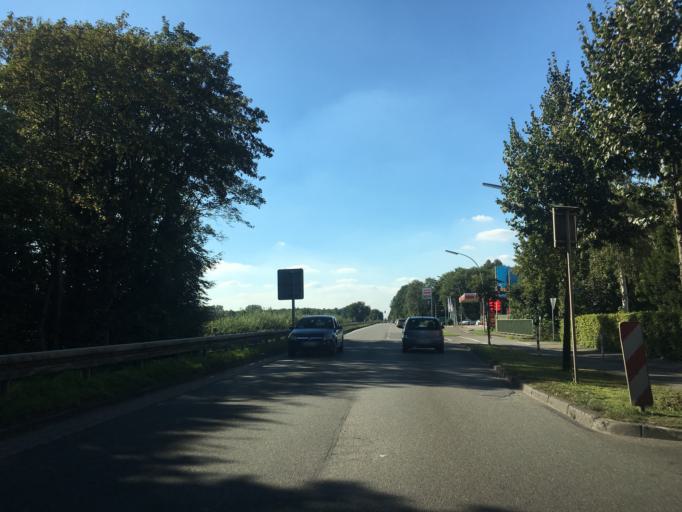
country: DE
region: North Rhine-Westphalia
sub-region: Regierungsbezirk Munster
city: Beelen
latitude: 51.9036
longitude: 8.1898
